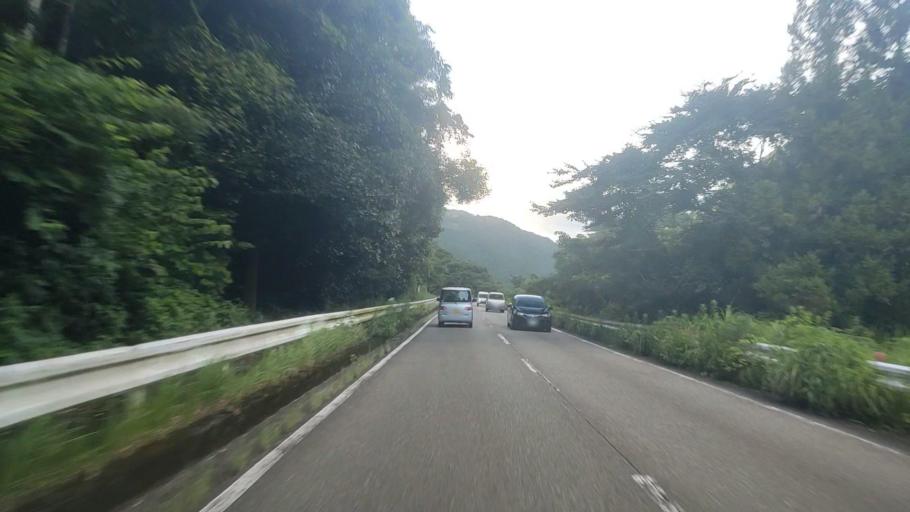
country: JP
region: Wakayama
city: Tanabe
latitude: 33.7644
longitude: 135.5002
